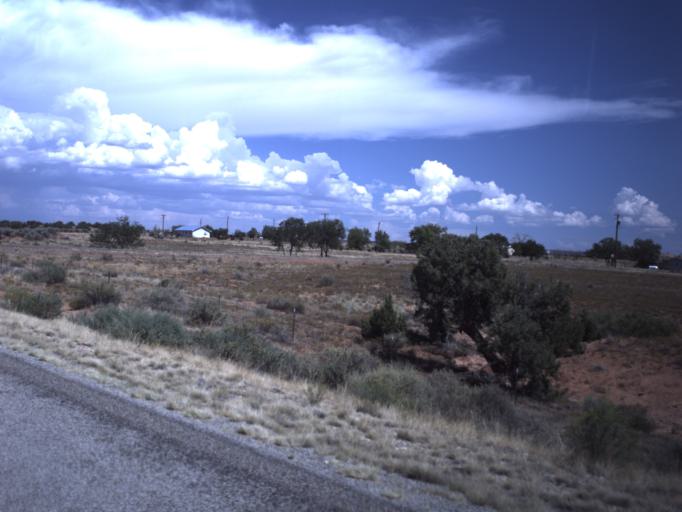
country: US
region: Utah
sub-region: San Juan County
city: Blanding
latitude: 37.4730
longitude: -109.4669
